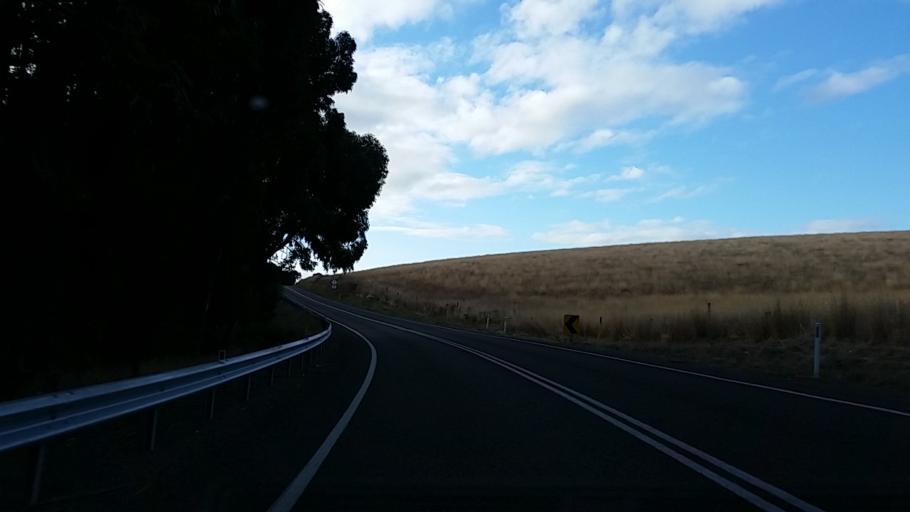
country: AU
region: South Australia
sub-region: Yankalilla
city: Normanville
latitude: -35.5618
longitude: 138.2004
